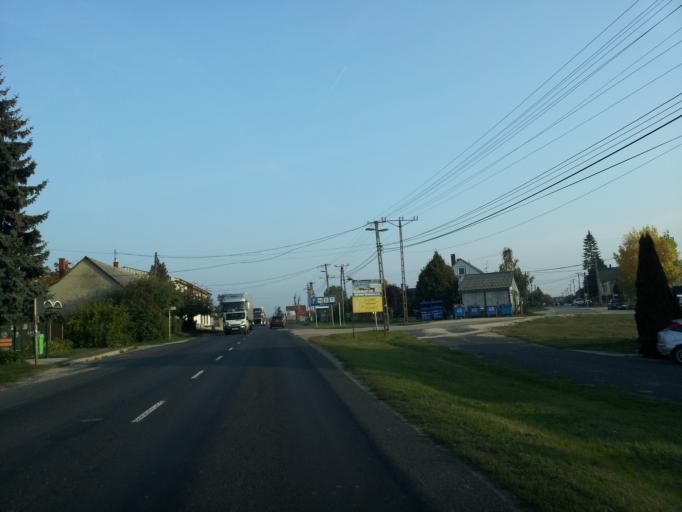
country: HU
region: Komarom-Esztergom
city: Kisber
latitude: 47.5084
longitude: 18.0123
